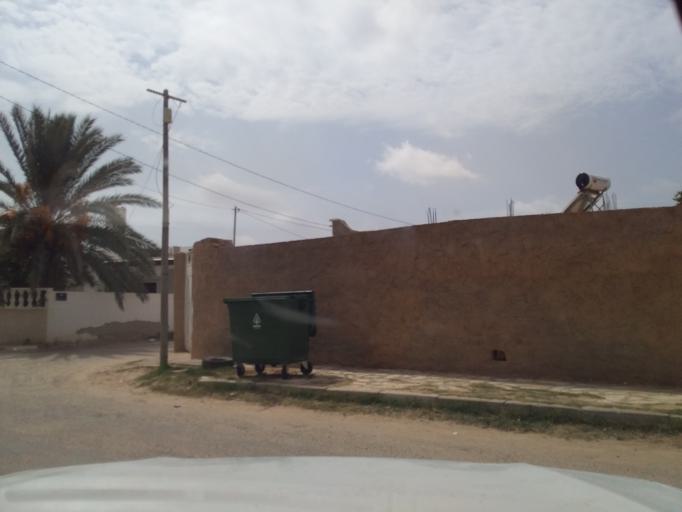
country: TN
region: Qabis
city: Gabes
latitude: 33.6164
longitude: 10.2942
